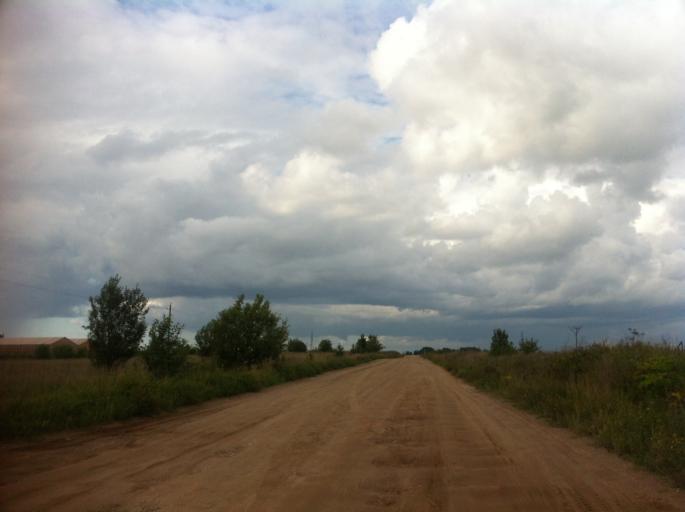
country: RU
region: Pskov
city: Izborsk
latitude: 57.8236
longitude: 27.9794
